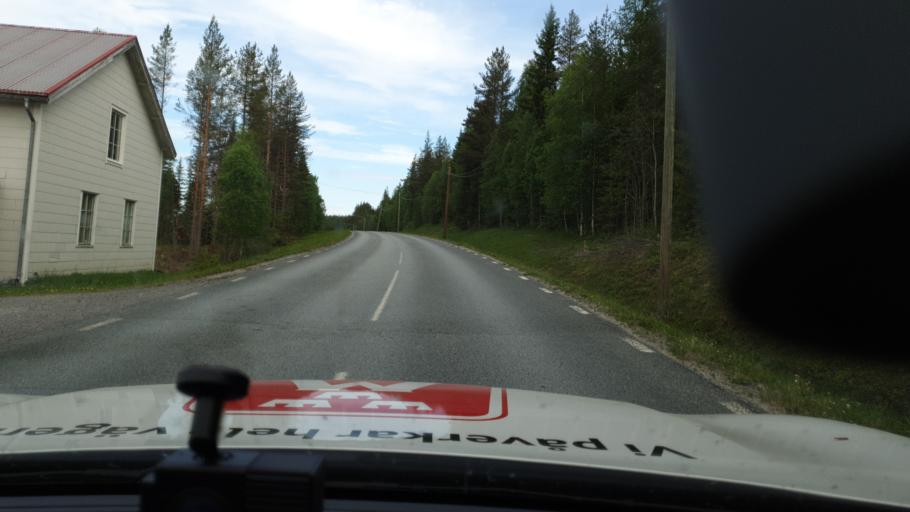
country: SE
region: Vaesterbotten
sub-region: Lycksele Kommun
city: Soderfors
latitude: 65.0875
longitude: 18.3265
